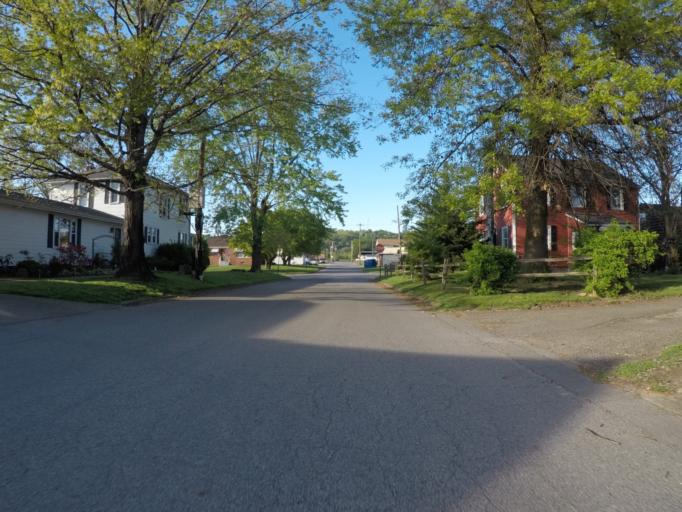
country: US
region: West Virginia
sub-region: Wayne County
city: Ceredo
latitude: 38.3964
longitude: -82.5671
